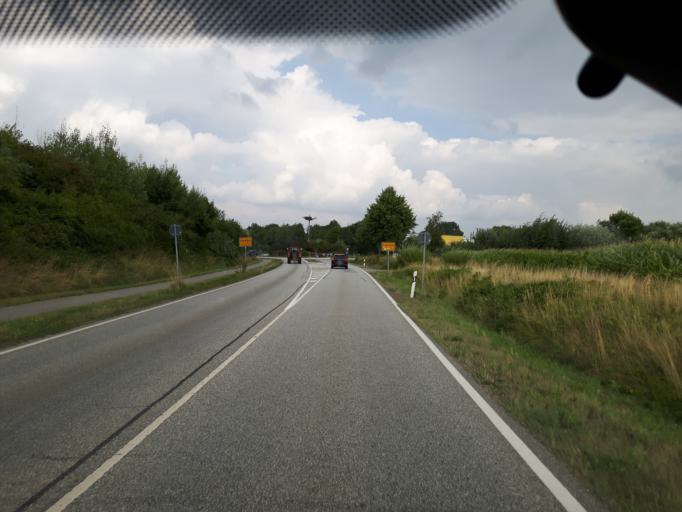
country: DE
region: Schleswig-Holstein
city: Goosefeld
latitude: 54.4450
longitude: 9.8256
